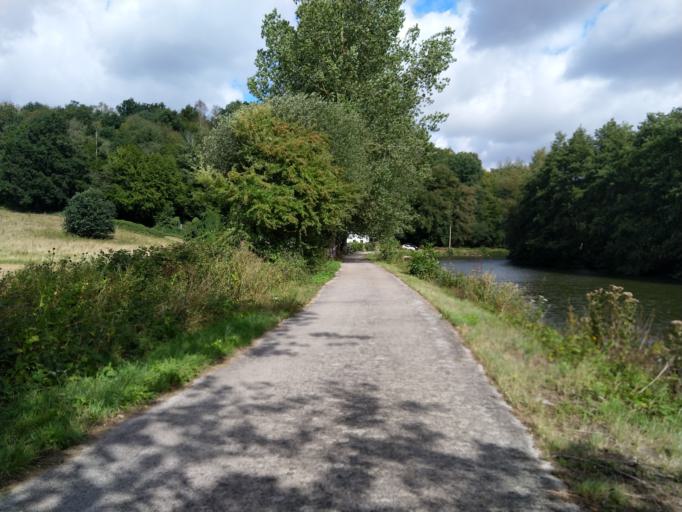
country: BE
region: Wallonia
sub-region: Province du Hainaut
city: Lobbes
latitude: 50.3473
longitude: 4.2478
